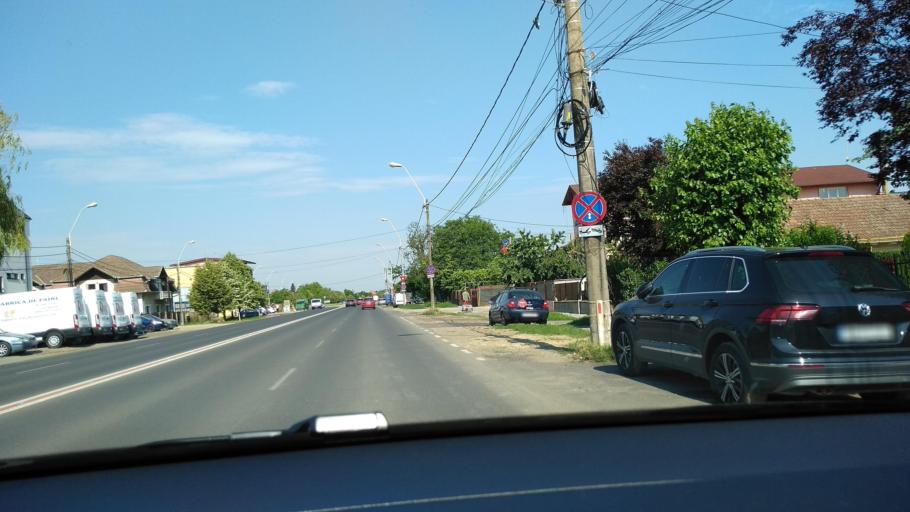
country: RO
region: Timis
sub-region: Comuna Ghiroda
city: Ghiroda
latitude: 45.7265
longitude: 21.2795
